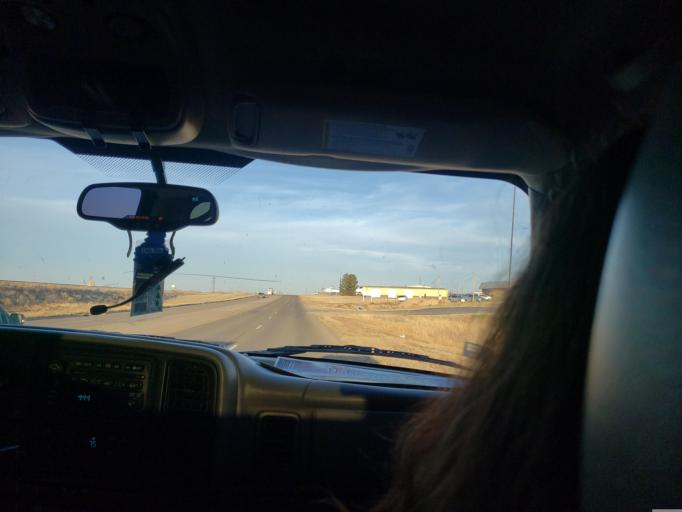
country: US
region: Oklahoma
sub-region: Texas County
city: Guymon
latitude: 36.6934
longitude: -101.4622
